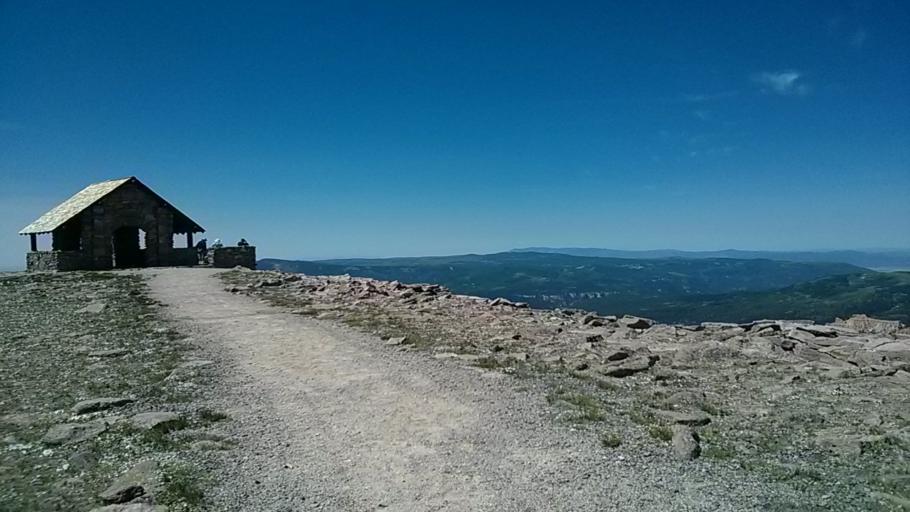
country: US
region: Utah
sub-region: Iron County
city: Parowan
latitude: 37.6815
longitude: -112.8310
